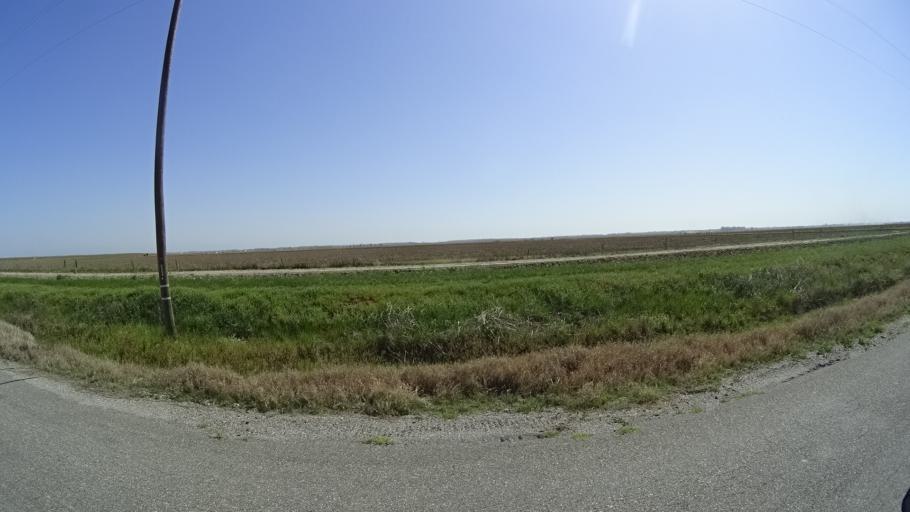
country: US
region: California
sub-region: Glenn County
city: Willows
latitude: 39.5085
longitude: -122.0653
